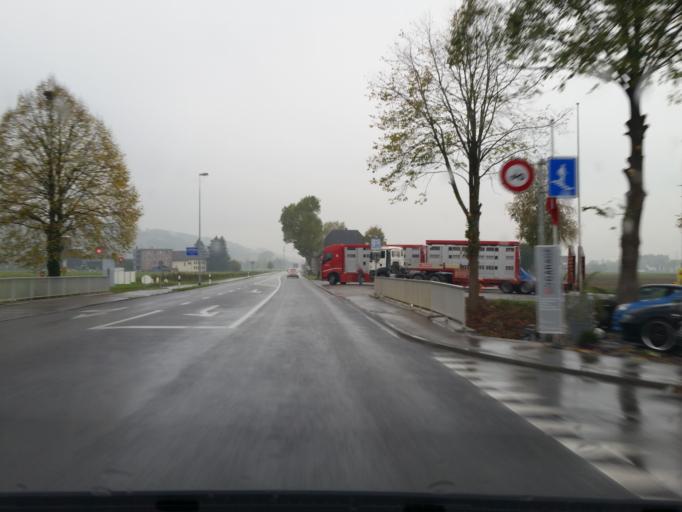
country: CH
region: Thurgau
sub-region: Weinfelden District
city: Wigoltingen
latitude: 47.5826
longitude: 9.0444
